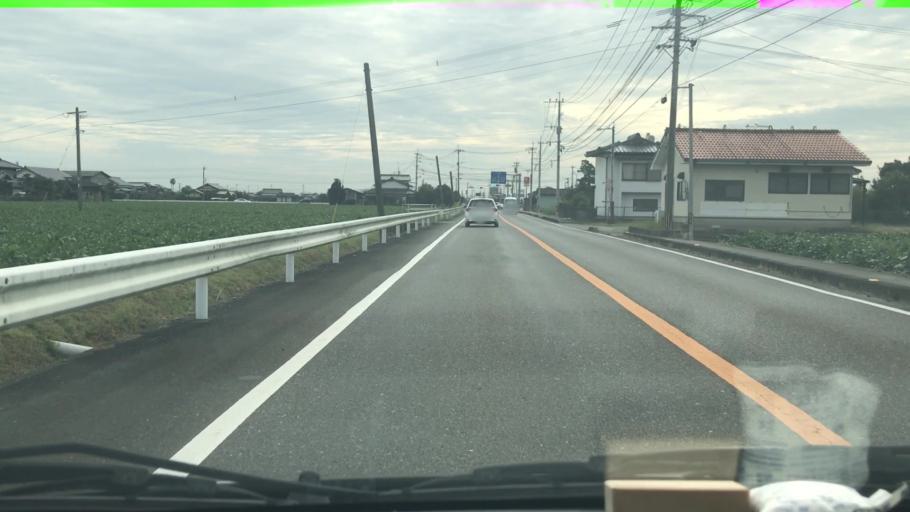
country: JP
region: Saga Prefecture
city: Takeocho-takeo
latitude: 33.1992
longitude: 130.1001
